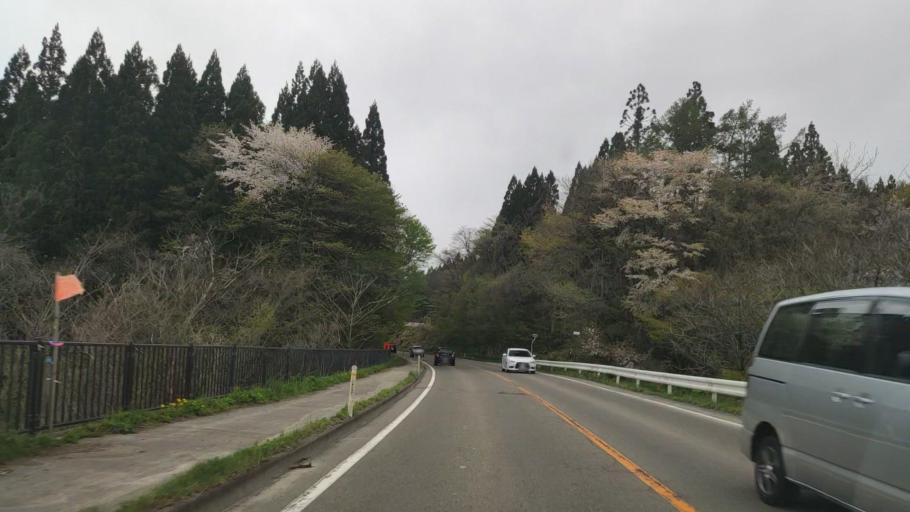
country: JP
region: Akita
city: Takanosu
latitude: 40.2156
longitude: 140.2974
